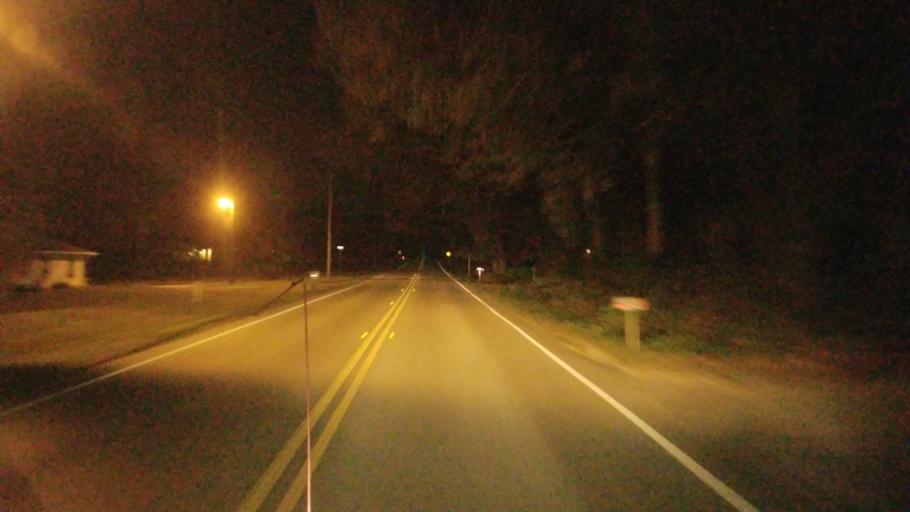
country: US
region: Florida
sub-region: Marion County
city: Ocala
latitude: 29.1675
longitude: -82.2518
